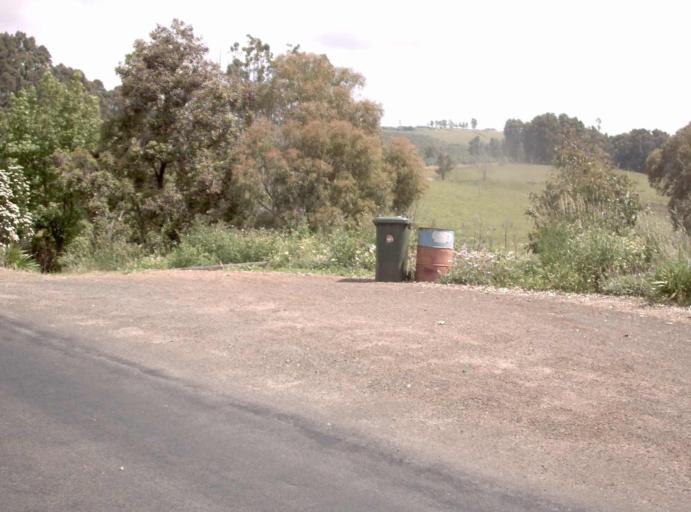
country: AU
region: Victoria
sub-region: Latrobe
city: Traralgon
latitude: -38.3485
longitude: 146.5683
